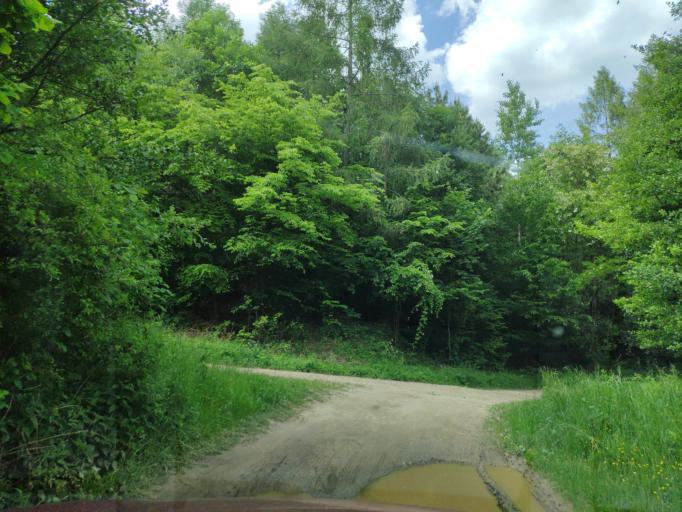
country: SK
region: Kosicky
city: Medzev
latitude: 48.7196
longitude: 20.9684
